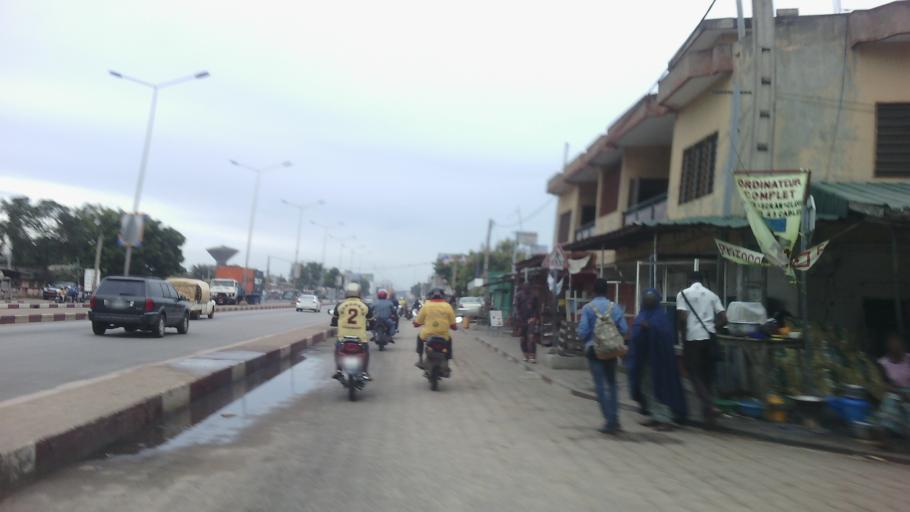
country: BJ
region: Littoral
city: Cotonou
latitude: 6.3649
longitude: 2.4173
